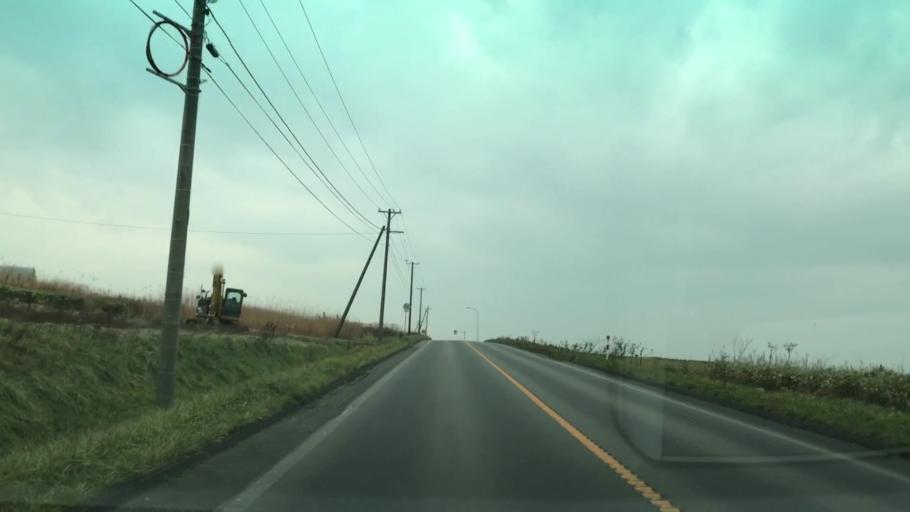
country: JP
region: Hokkaido
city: Ishikari
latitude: 43.3517
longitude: 141.4266
